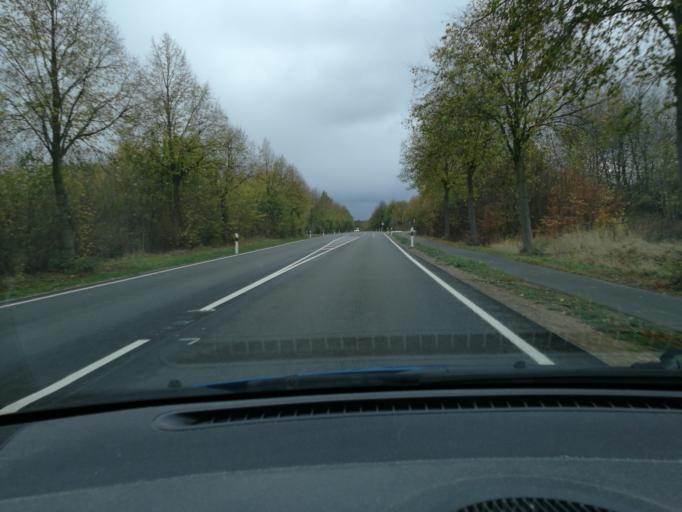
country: DE
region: Schleswig-Holstein
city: Harmsdorf
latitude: 53.6894
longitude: 10.7295
